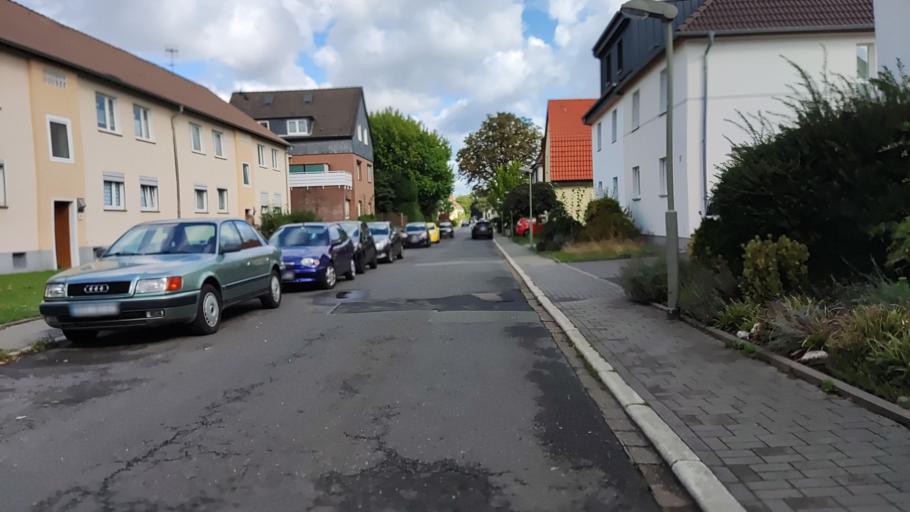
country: DE
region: North Rhine-Westphalia
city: Bochum-Hordel
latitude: 51.5191
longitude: 7.1860
